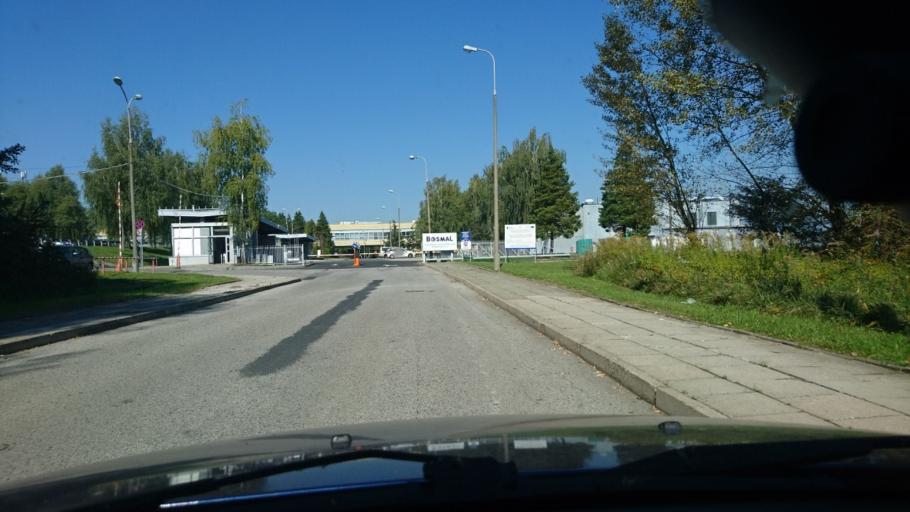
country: PL
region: Silesian Voivodeship
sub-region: Bielsko-Biala
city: Bielsko-Biala
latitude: 49.8417
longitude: 19.0293
